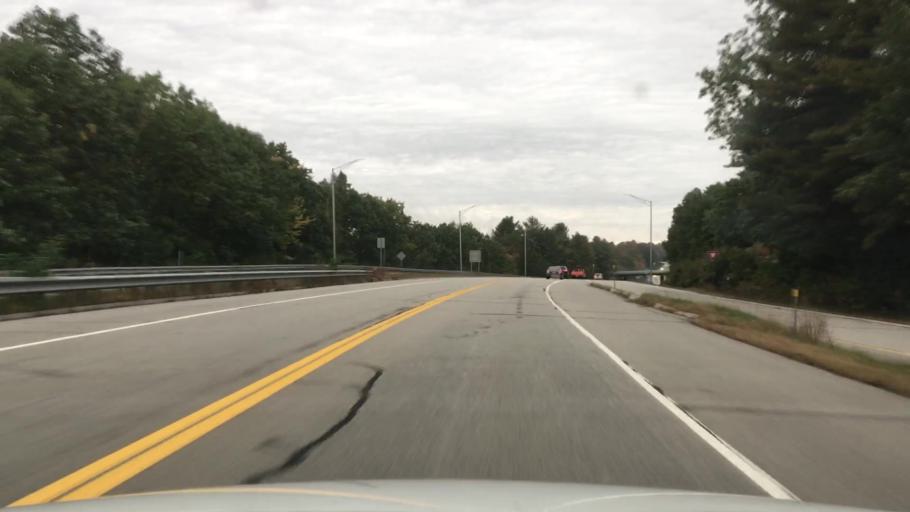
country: US
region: New Hampshire
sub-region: Strafford County
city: Durham
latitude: 43.1397
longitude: -70.9134
